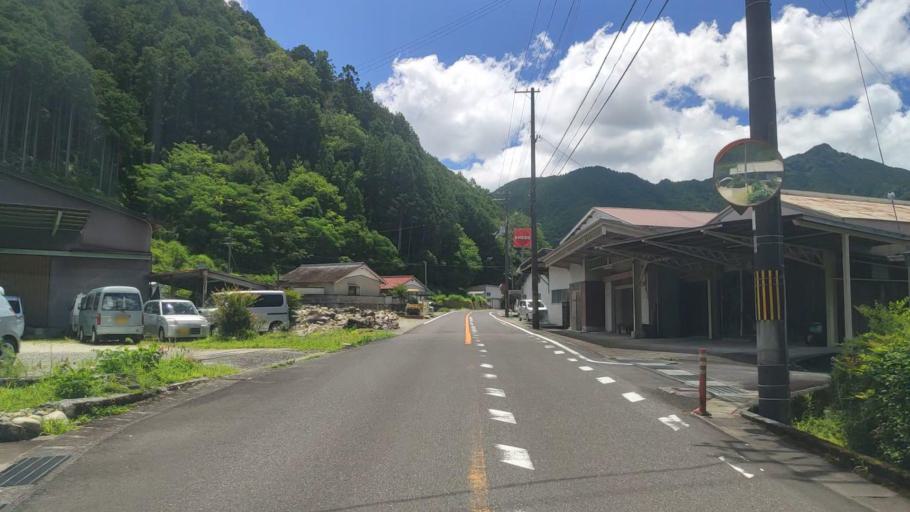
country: JP
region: Mie
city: Owase
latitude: 33.9838
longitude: 136.0488
